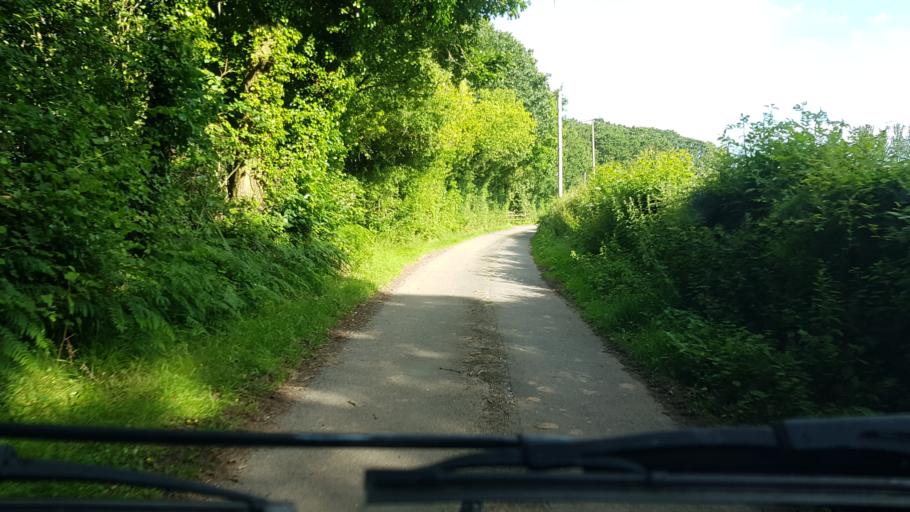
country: GB
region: England
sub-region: Worcestershire
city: Bewdley
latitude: 52.3368
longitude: -2.3211
